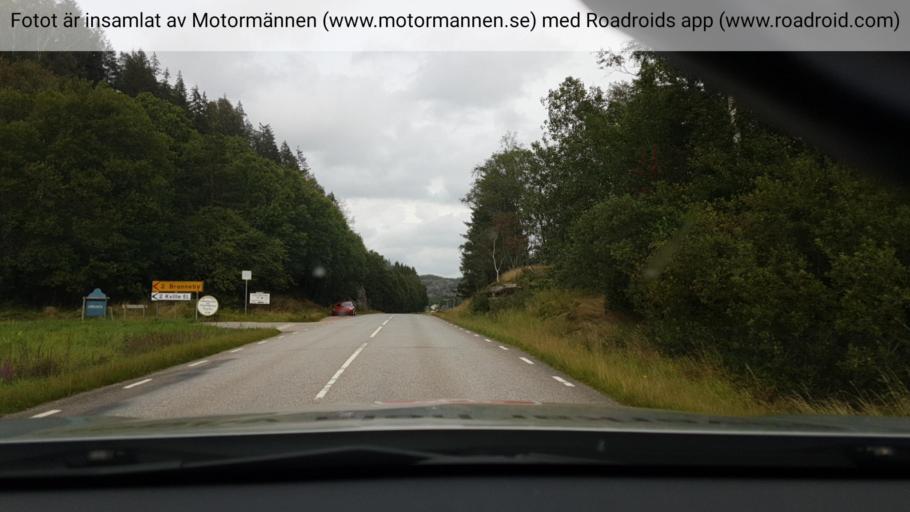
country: SE
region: Vaestra Goetaland
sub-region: Lysekils Kommun
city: Brastad
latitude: 58.5565
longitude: 11.4580
